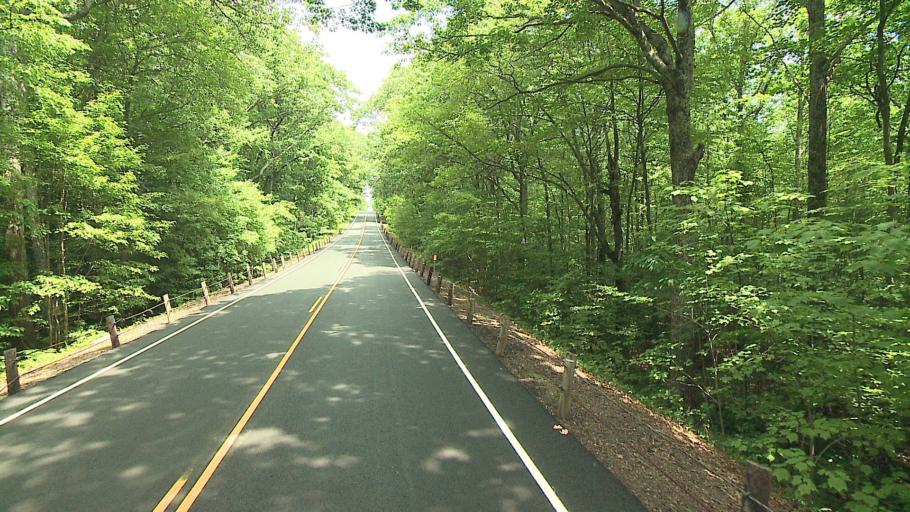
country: US
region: Massachusetts
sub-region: Hampden County
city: Granville
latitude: 42.0197
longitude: -72.8898
